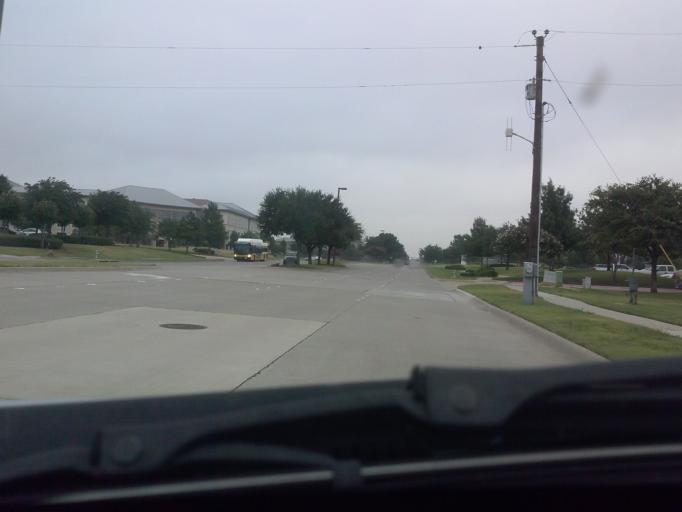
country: US
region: Texas
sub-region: Denton County
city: The Colony
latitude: 33.0672
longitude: -96.8185
